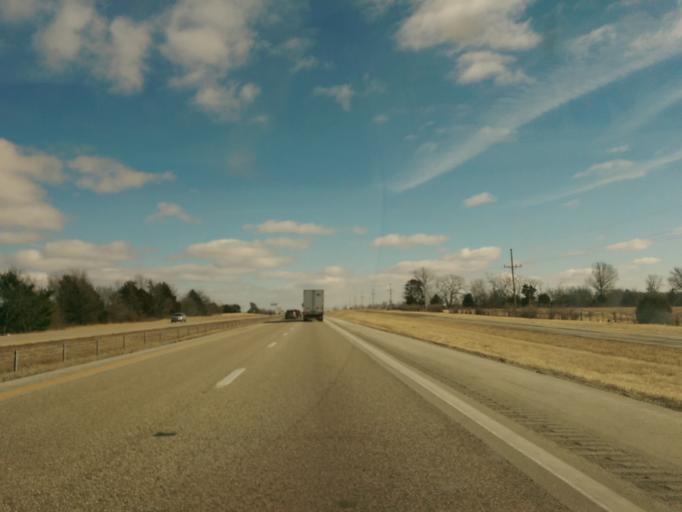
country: US
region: Missouri
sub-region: Montgomery County
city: Montgomery City
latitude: 38.9065
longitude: -91.5168
